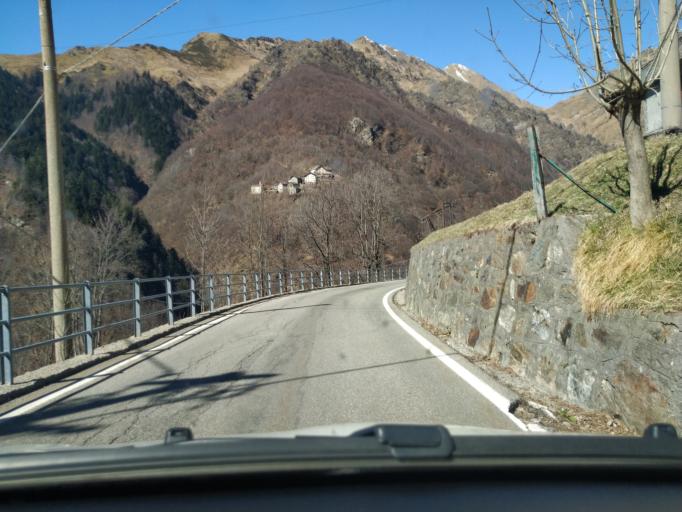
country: IT
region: Piedmont
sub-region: Provincia di Vercelli
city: Rimella
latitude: 45.9078
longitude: 8.1816
